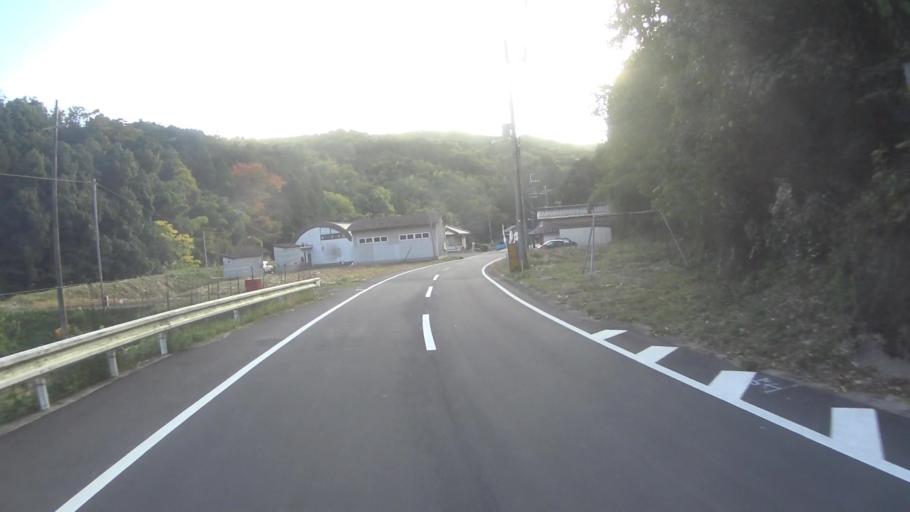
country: JP
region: Kyoto
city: Miyazu
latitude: 35.4574
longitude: 135.2298
